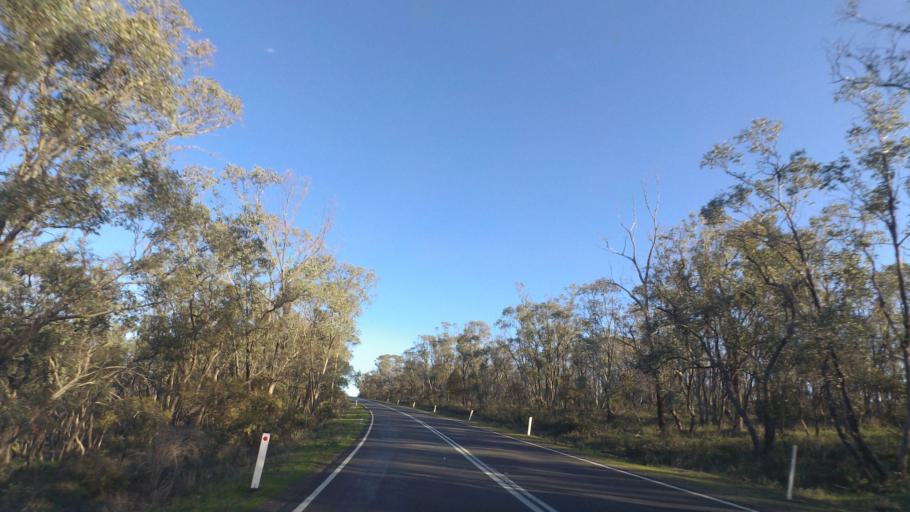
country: AU
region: Victoria
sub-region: Greater Bendigo
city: Kennington
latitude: -36.9241
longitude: 144.4897
